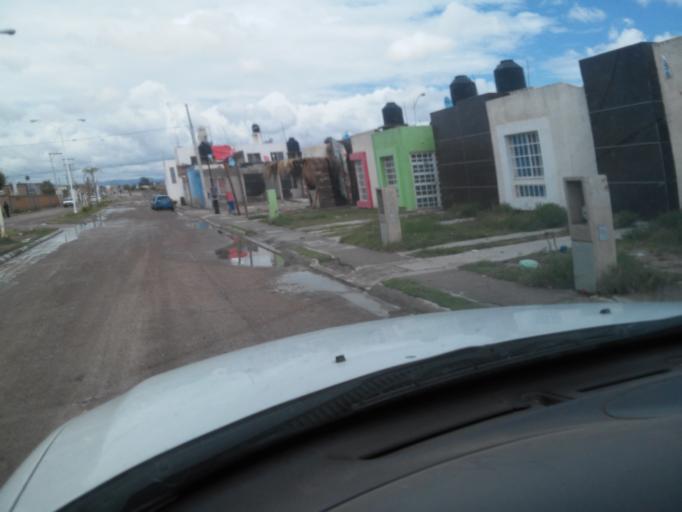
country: MX
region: Durango
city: Victoria de Durango
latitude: 24.0228
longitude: -104.6140
